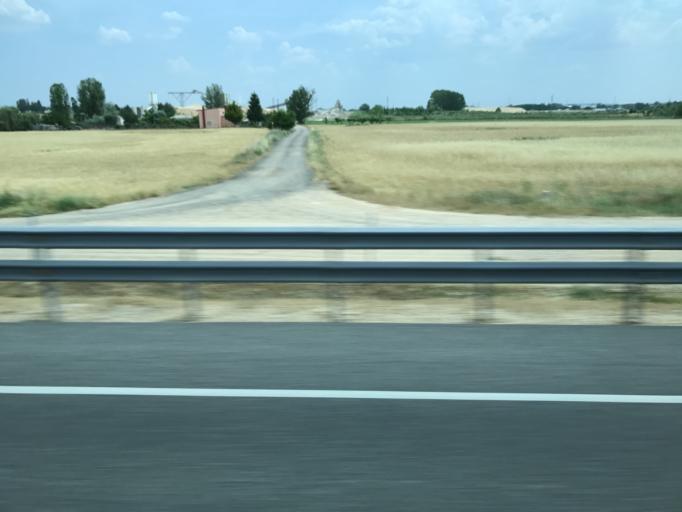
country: ES
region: Castille and Leon
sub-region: Provincia de Burgos
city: Villalba de Duero
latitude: 41.6753
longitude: -3.7291
